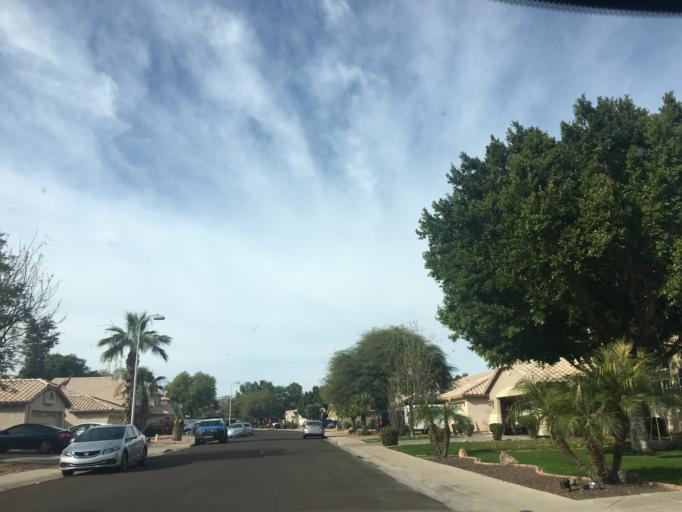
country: US
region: Arizona
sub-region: Maricopa County
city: Gilbert
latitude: 33.3475
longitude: -111.8087
